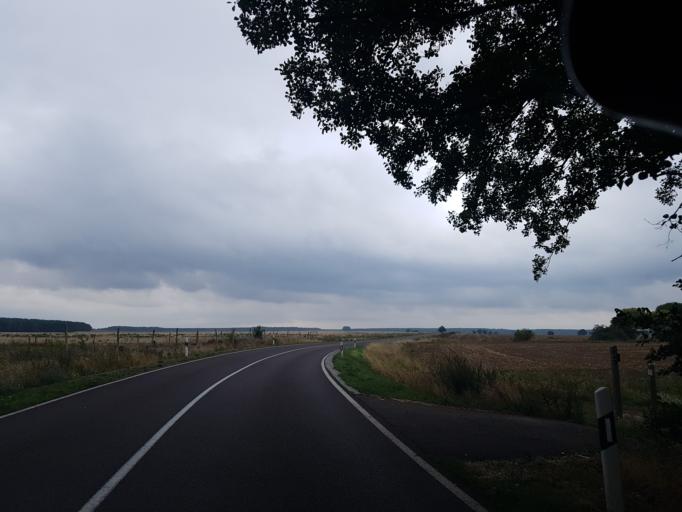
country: DE
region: Saxony-Anhalt
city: Loburg
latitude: 52.1666
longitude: 12.1178
